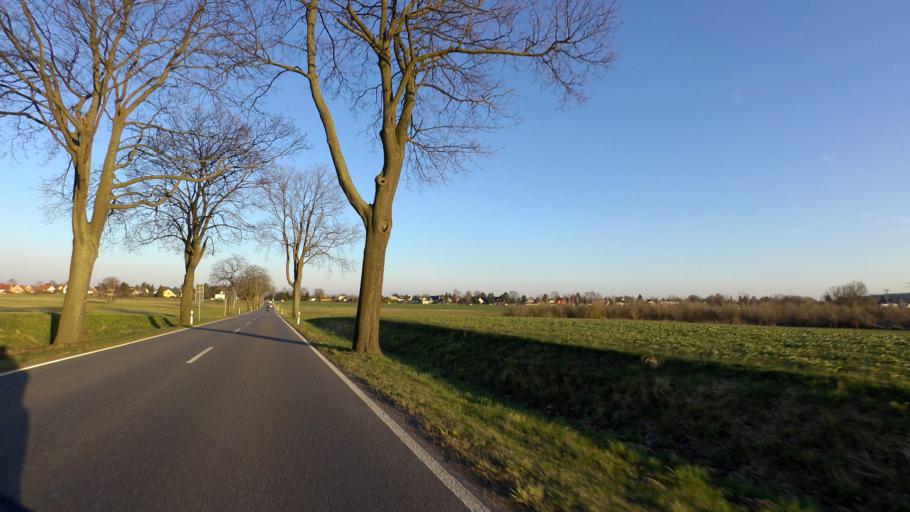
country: DE
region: Brandenburg
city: Ahrensfelde
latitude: 52.5753
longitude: 13.5882
